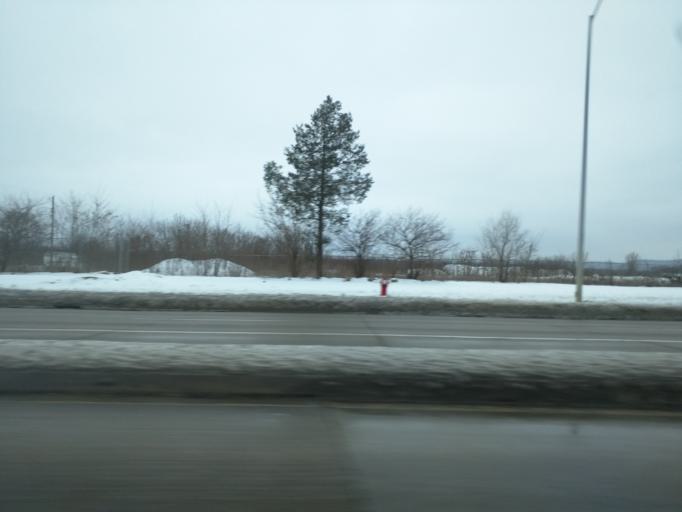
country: US
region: Wisconsin
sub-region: La Crosse County
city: La Crosse
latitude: 43.8223
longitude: -91.2492
